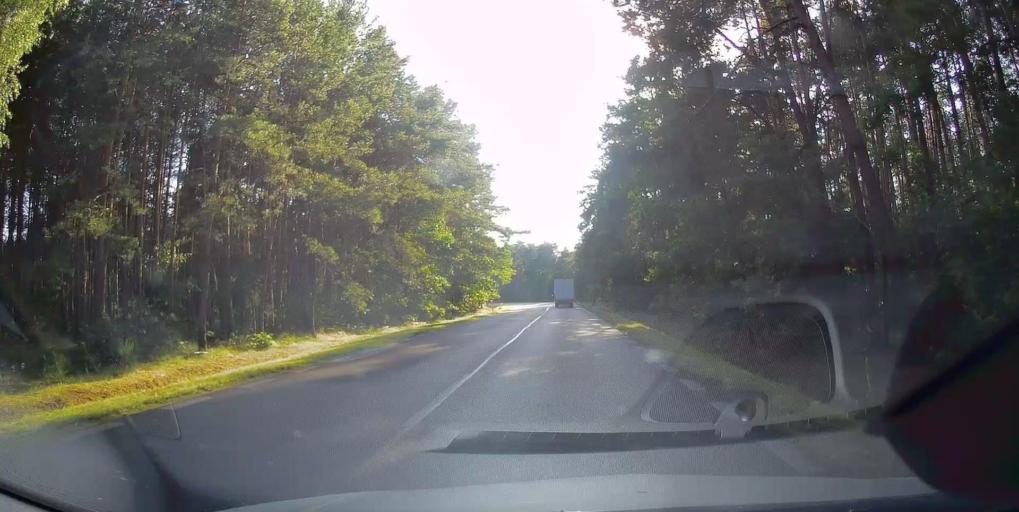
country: PL
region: Lodz Voivodeship
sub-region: Powiat rawski
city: Regnow
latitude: 51.7986
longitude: 20.3936
